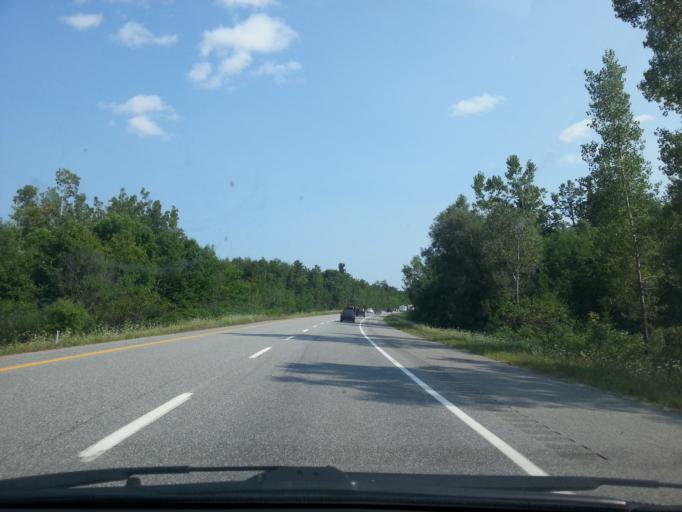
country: CA
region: Quebec
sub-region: Outaouais
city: Gatineau
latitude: 45.5298
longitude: -75.8247
